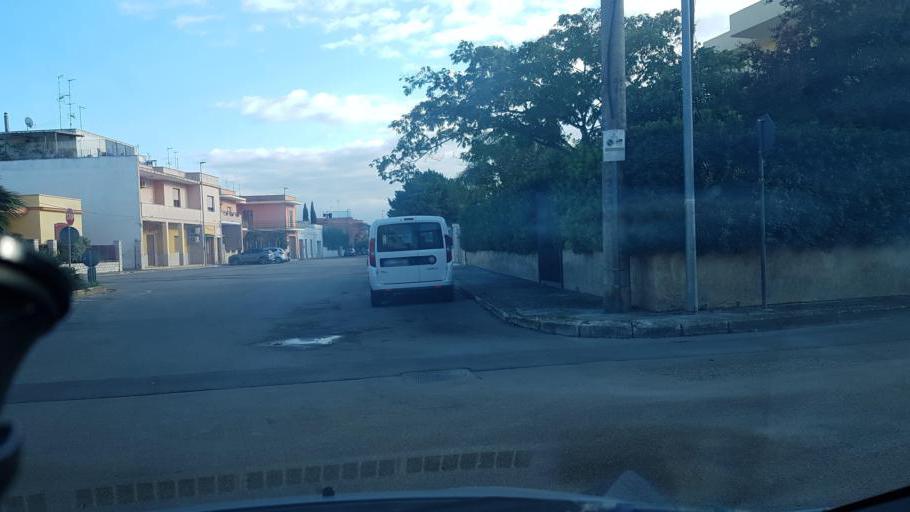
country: IT
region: Apulia
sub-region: Provincia di Lecce
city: Guagnano
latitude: 40.3994
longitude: 17.9476
